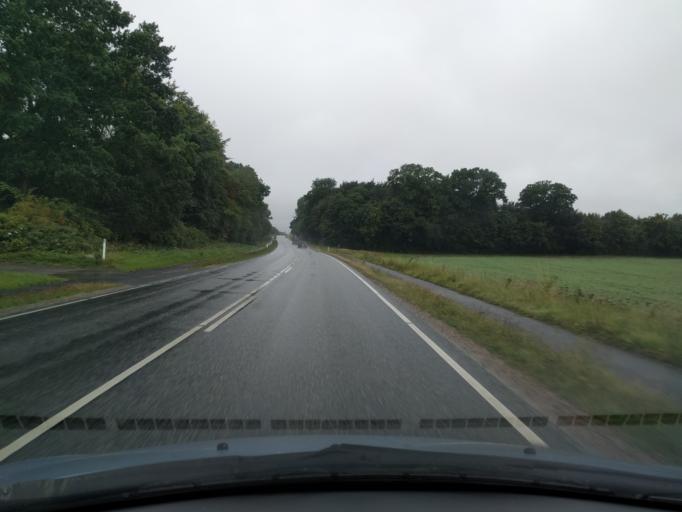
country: DK
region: Zealand
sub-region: Naestved Kommune
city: Fuglebjerg
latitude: 55.2782
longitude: 11.6172
